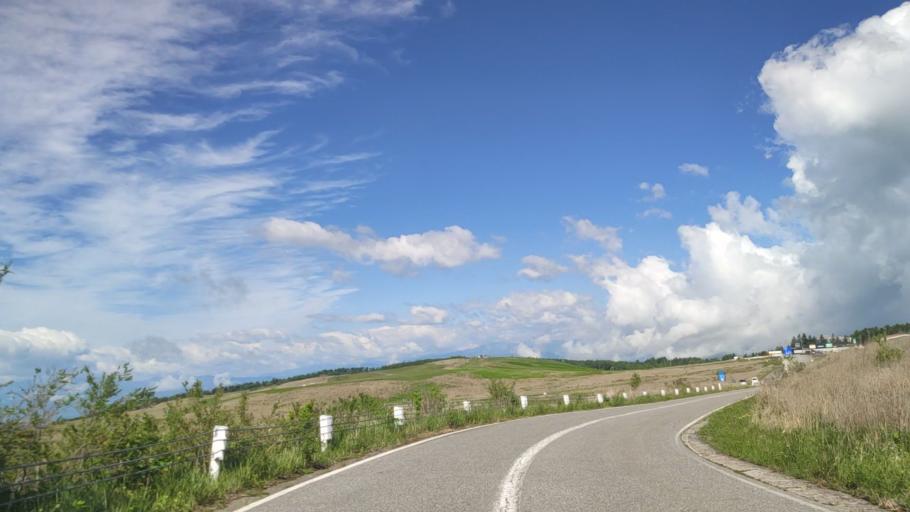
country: JP
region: Nagano
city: Suwa
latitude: 36.0894
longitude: 138.1716
